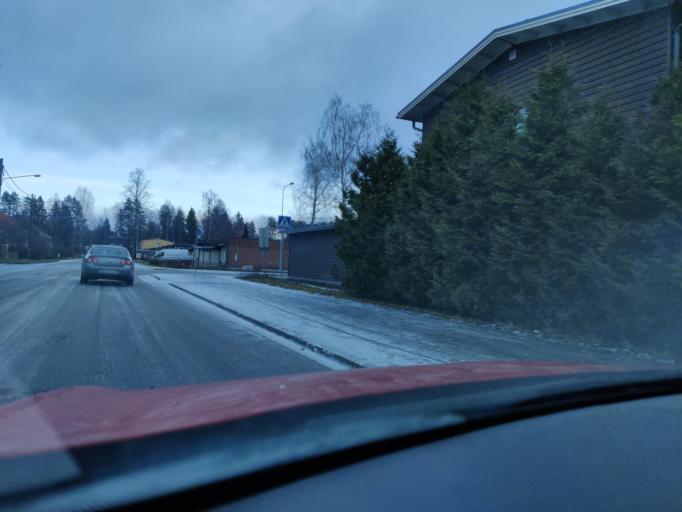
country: FI
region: Pirkanmaa
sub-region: Tampere
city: Nokia
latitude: 61.4641
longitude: 23.4866
